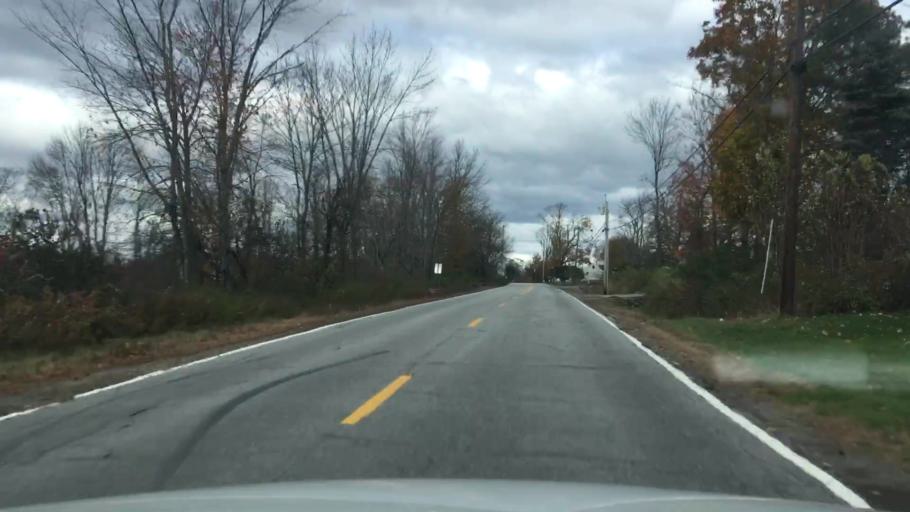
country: US
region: Maine
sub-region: Androscoggin County
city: Sabattus
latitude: 44.1529
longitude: -70.0811
